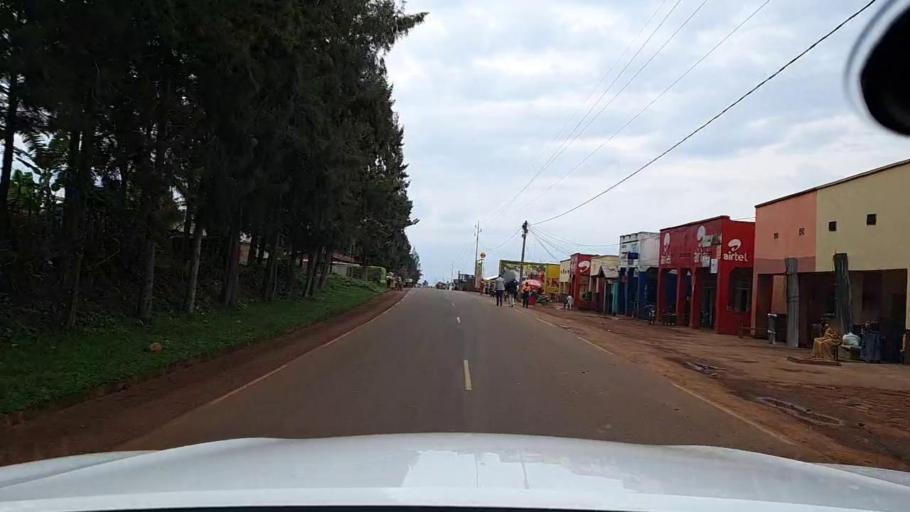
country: RW
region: Western Province
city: Cyangugu
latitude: -2.6379
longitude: 28.9523
